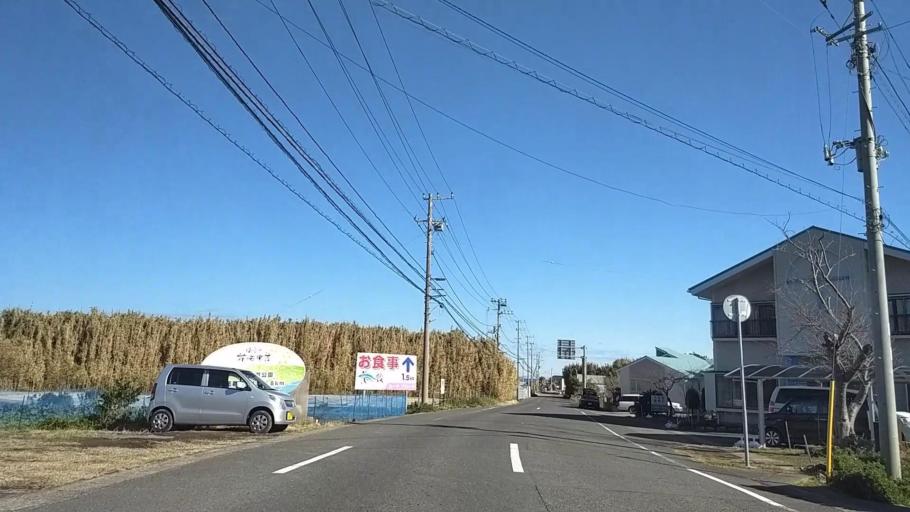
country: JP
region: Chiba
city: Tateyama
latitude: 34.9948
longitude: 139.9687
